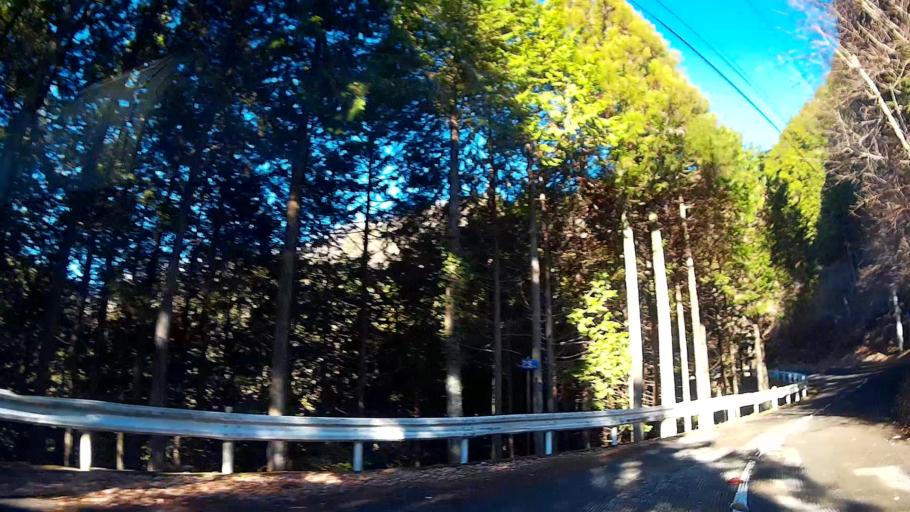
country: JP
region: Saitama
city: Chichibu
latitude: 35.9423
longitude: 139.1638
